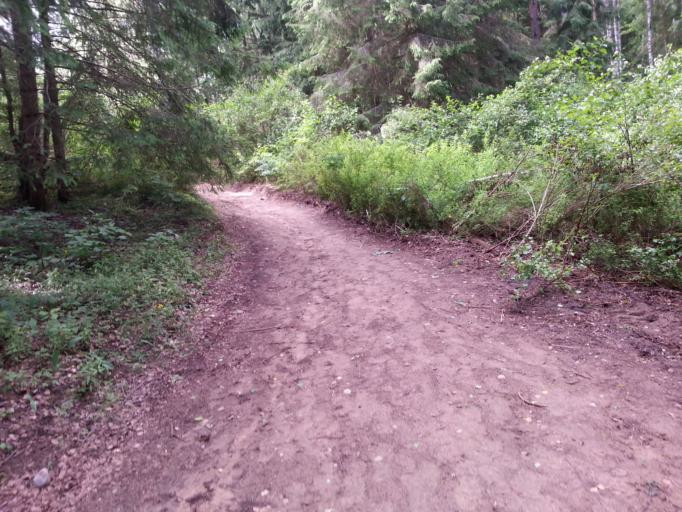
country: BY
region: Minsk
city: Svir
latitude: 54.9642
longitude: 26.3856
